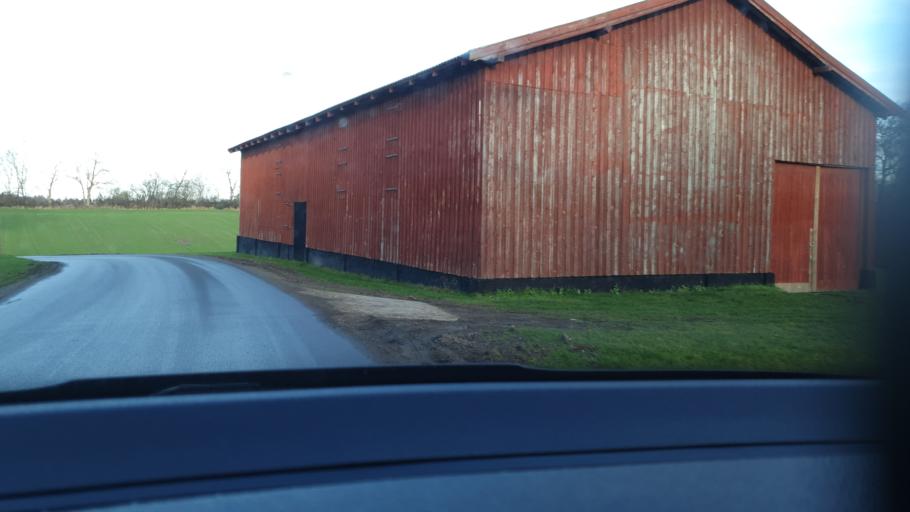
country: DK
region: Zealand
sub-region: Odsherred Kommune
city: Nykobing Sjaelland
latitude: 55.9226
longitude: 11.6379
